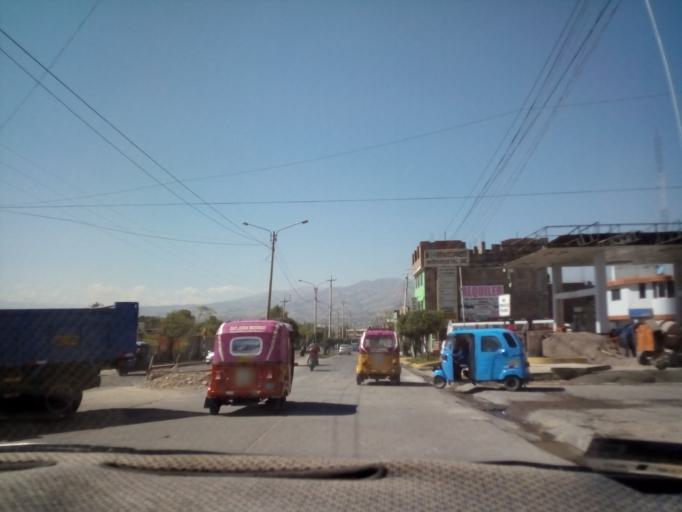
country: PE
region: Ayacucho
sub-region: Provincia de Huamanga
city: Ayacucho
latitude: -13.1464
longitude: -74.2247
